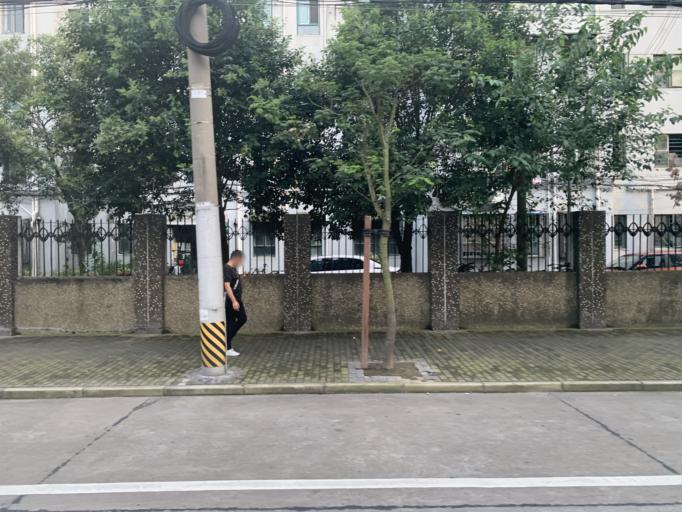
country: CN
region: Shanghai Shi
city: Huamu
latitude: 31.2453
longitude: 121.5695
